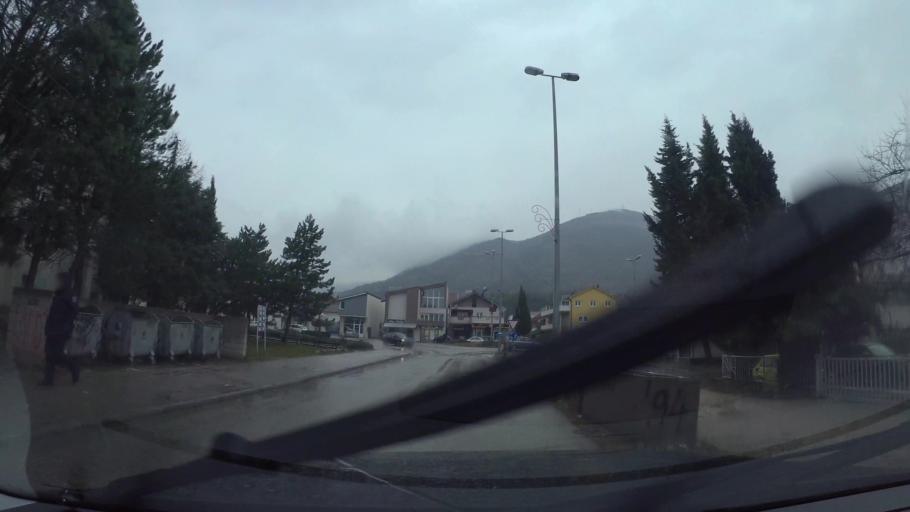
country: BA
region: Federation of Bosnia and Herzegovina
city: Cim
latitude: 43.3521
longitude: 17.7931
